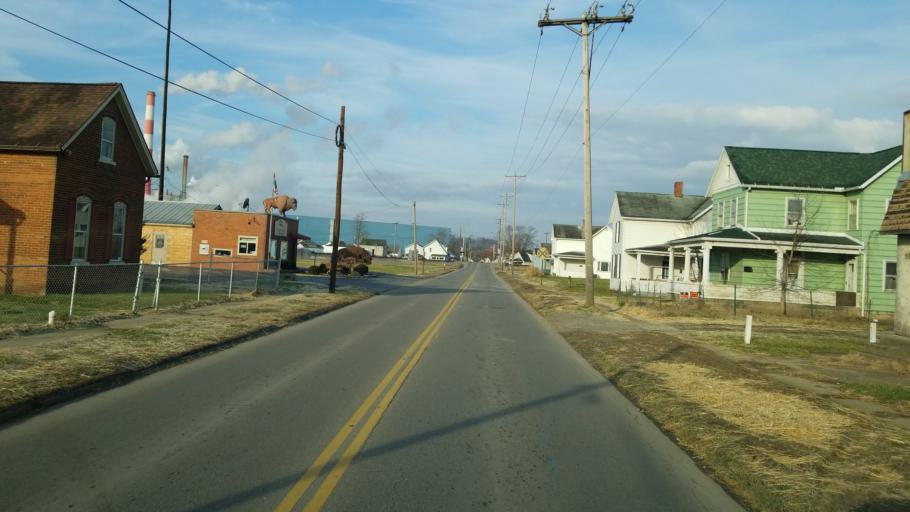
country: US
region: Ohio
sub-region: Ross County
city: Chillicothe
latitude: 39.3256
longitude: -82.9652
